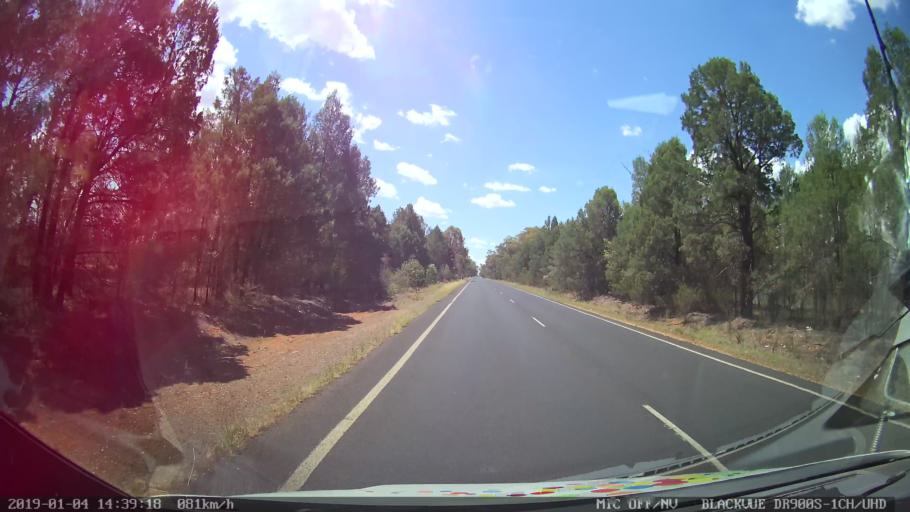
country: AU
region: New South Wales
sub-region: Dubbo Municipality
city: Dubbo
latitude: -32.1665
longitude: 148.6327
